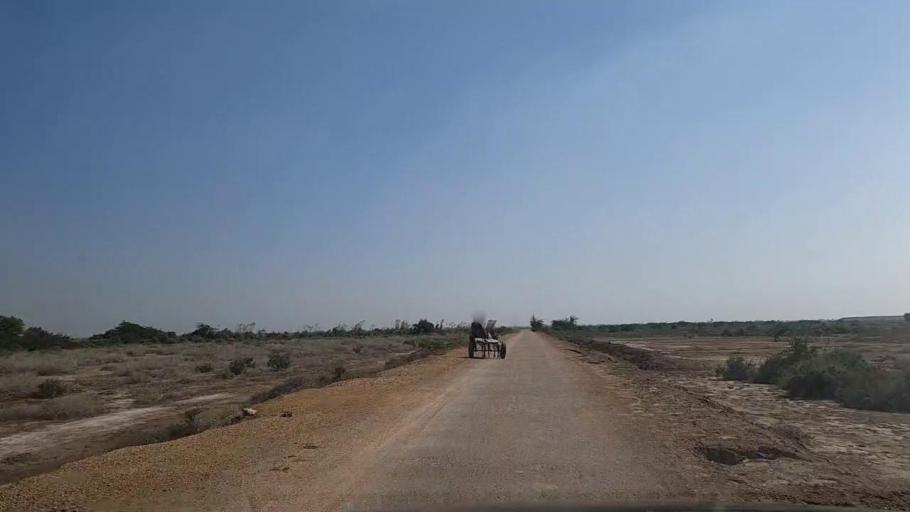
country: PK
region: Sindh
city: Daro Mehar
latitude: 24.8021
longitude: 68.0774
